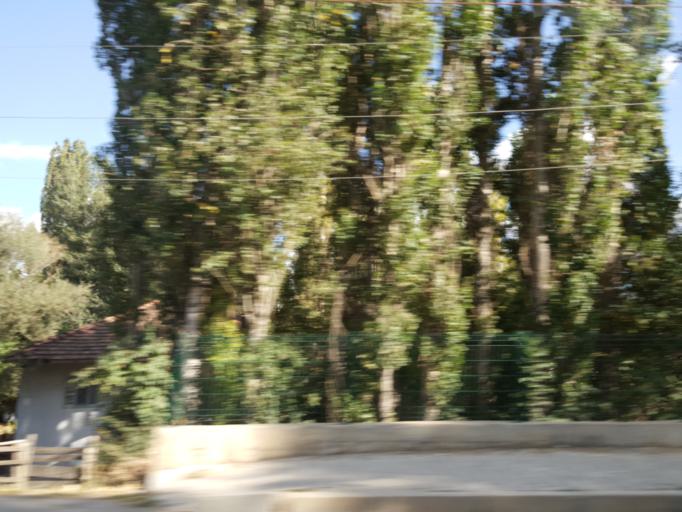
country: TR
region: Tokat
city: Sulusaray
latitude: 39.9920
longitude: 36.0834
